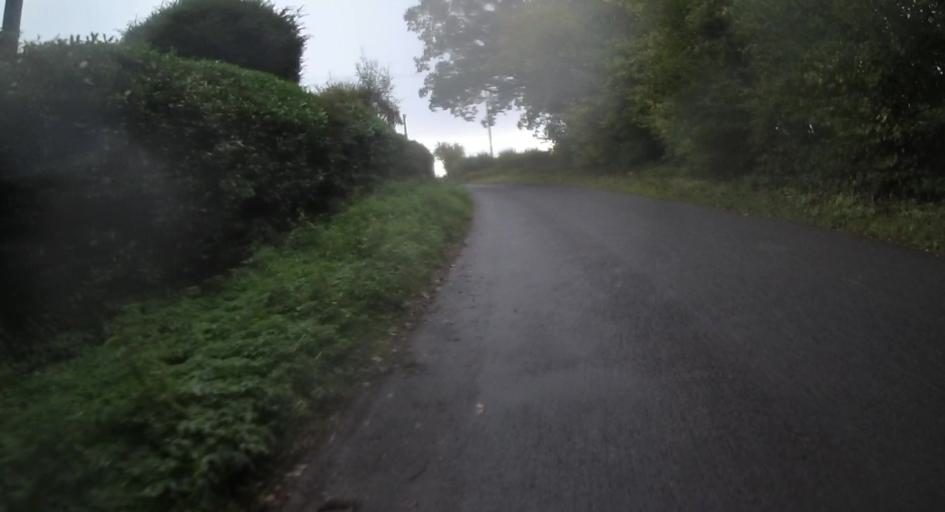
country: GB
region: England
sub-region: Hampshire
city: Tadley
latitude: 51.3072
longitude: -1.1345
